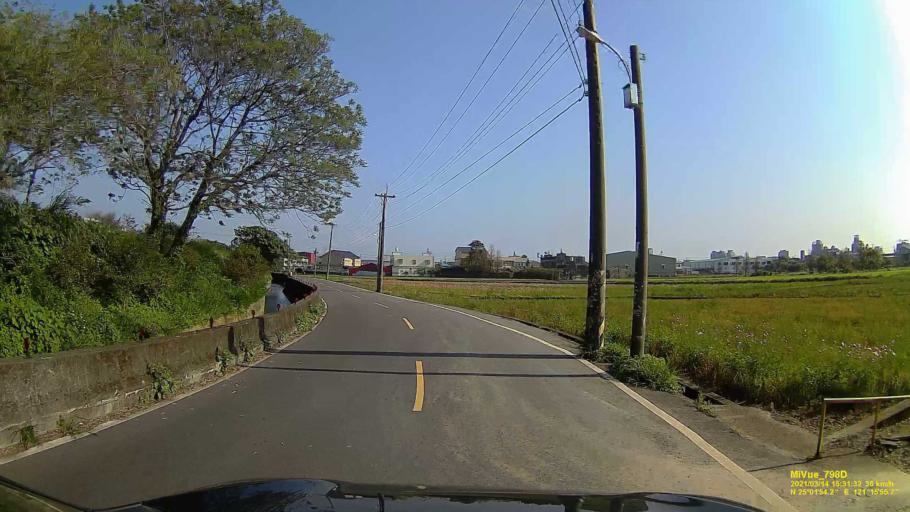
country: TW
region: Taiwan
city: Taoyuan City
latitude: 25.0317
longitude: 121.2657
